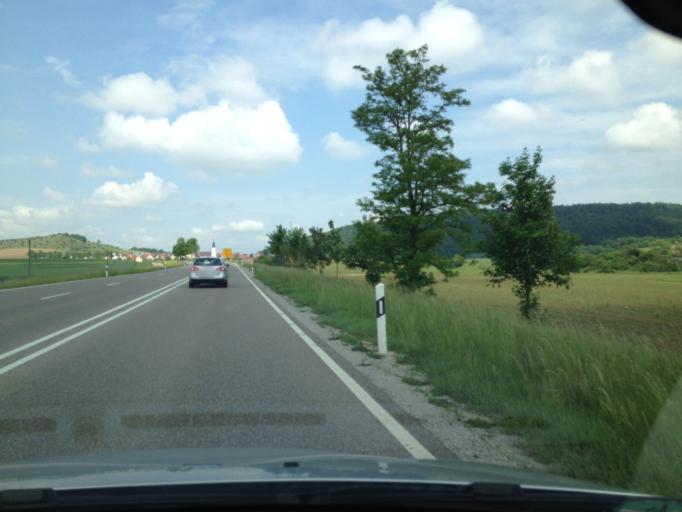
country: DE
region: Bavaria
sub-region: Swabia
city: Harburg
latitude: 48.7939
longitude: 10.6630
